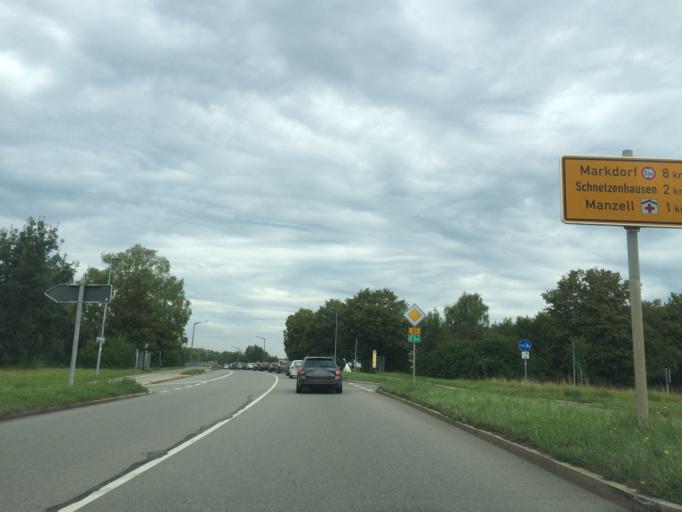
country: DE
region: Baden-Wuerttemberg
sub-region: Tuebingen Region
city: Friedrichshafen
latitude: 47.6639
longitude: 9.4312
